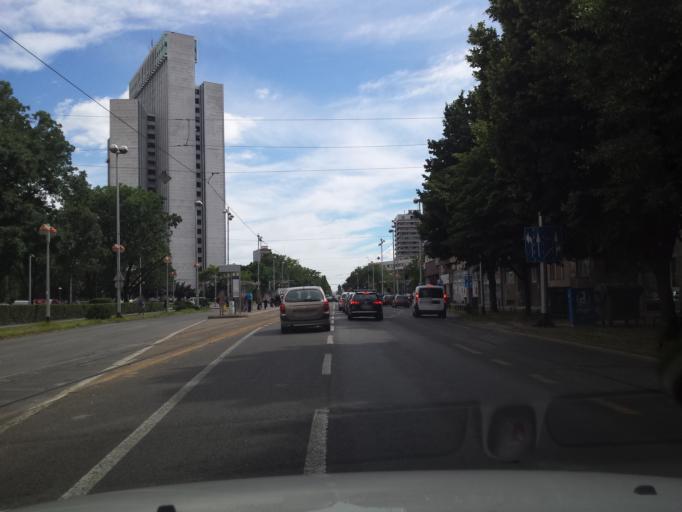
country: HR
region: Grad Zagreb
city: Zagreb - Centar
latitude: 45.8005
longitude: 15.9629
